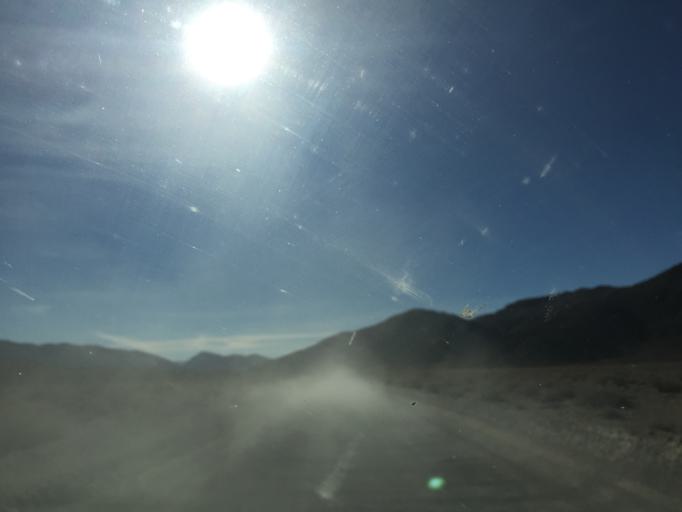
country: US
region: California
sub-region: Inyo County
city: Lone Pine
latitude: 36.8277
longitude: -117.5073
